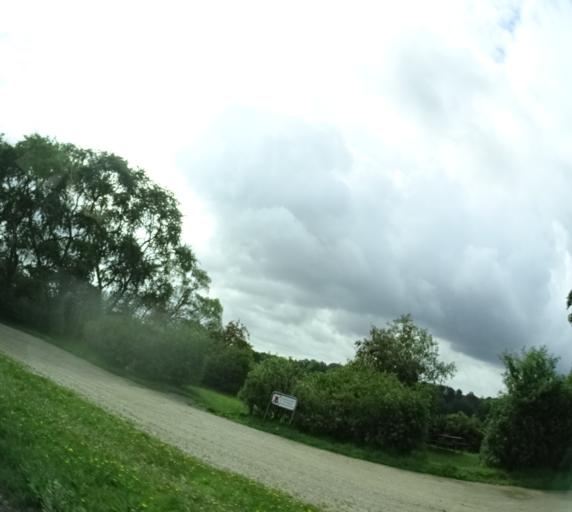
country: DK
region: Central Jutland
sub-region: Syddjurs Kommune
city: Ryomgard
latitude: 56.4063
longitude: 10.5323
